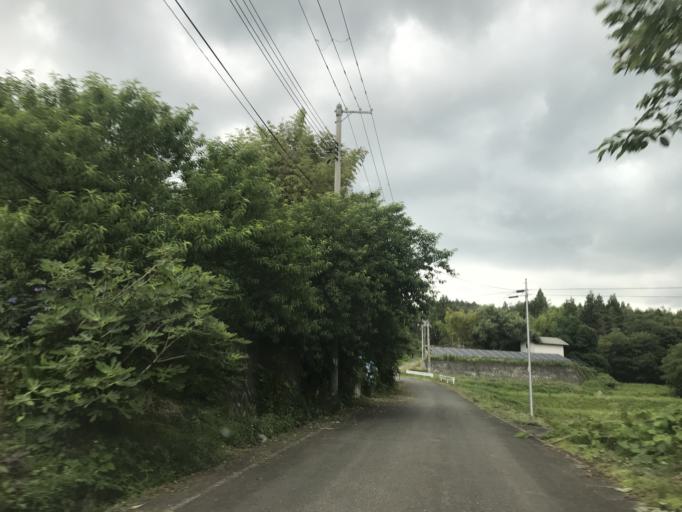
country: JP
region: Iwate
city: Ichinoseki
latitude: 38.9530
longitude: 141.0478
